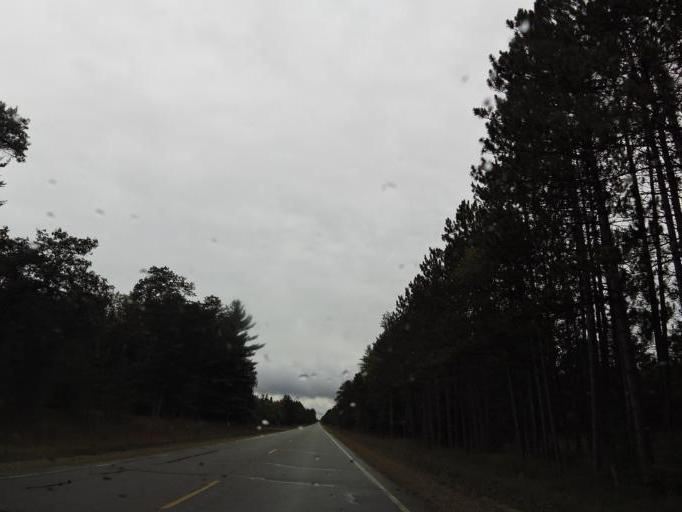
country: US
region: Michigan
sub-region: Roscommon County
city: Roscommon
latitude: 44.4647
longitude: -84.5351
